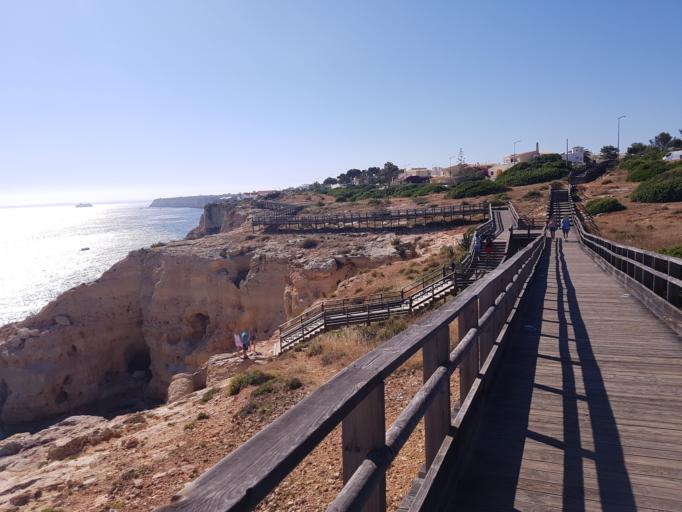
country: PT
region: Faro
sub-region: Lagoa
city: Carvoeiro
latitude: 37.0935
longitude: -8.4673
